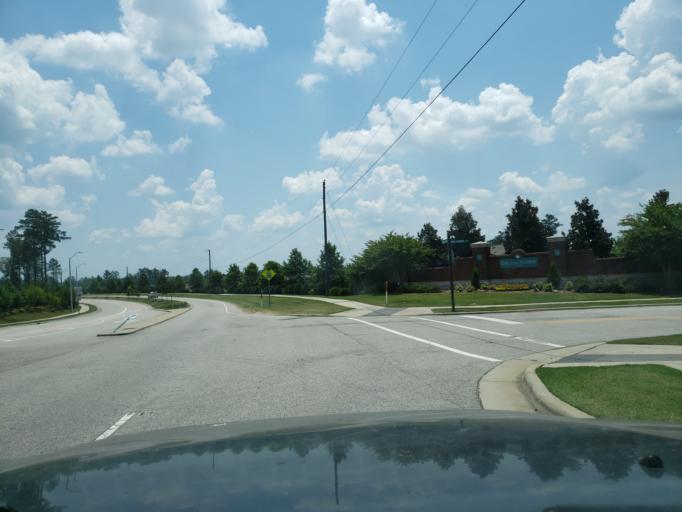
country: US
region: North Carolina
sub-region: Wake County
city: Green Level
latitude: 35.8443
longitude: -78.9130
